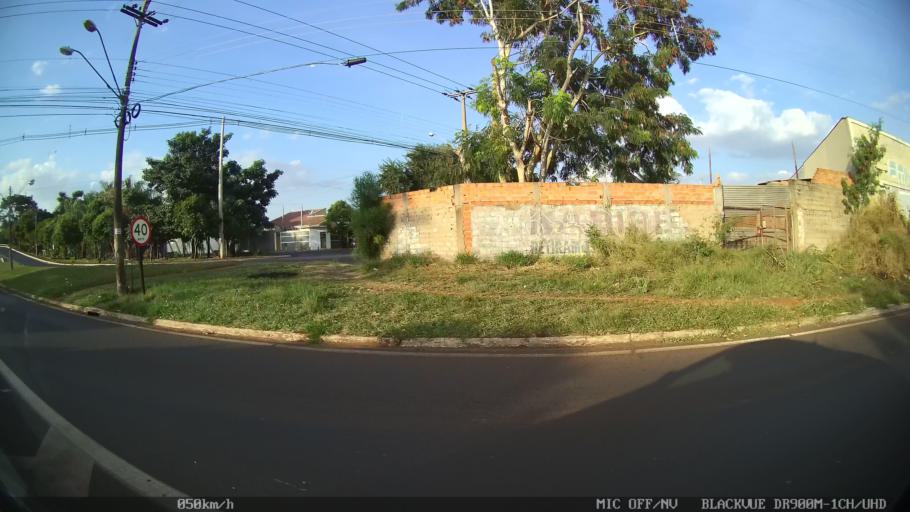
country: BR
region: Sao Paulo
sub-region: Ribeirao Preto
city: Ribeirao Preto
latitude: -21.1236
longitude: -47.7860
